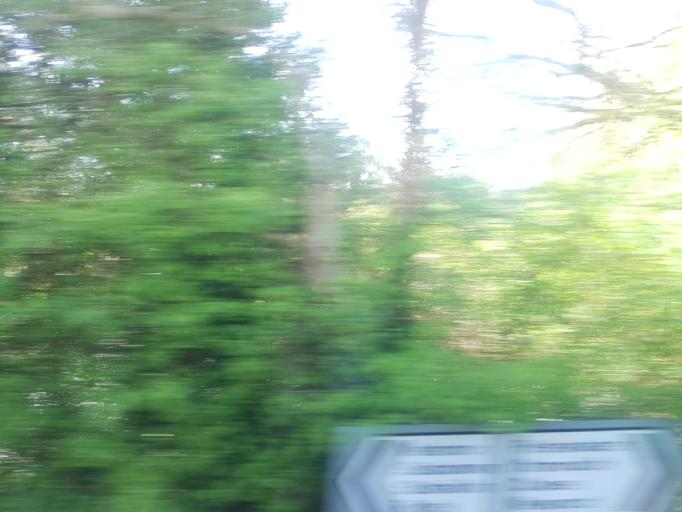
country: GB
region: England
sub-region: Isle of Wight
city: Ryde
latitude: 50.7265
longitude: -1.2133
